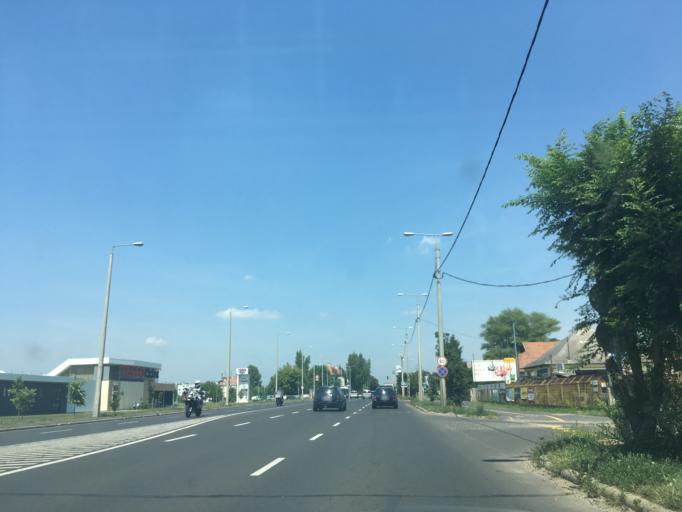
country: HU
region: Hajdu-Bihar
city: Debrecen
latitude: 47.5016
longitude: 21.6311
